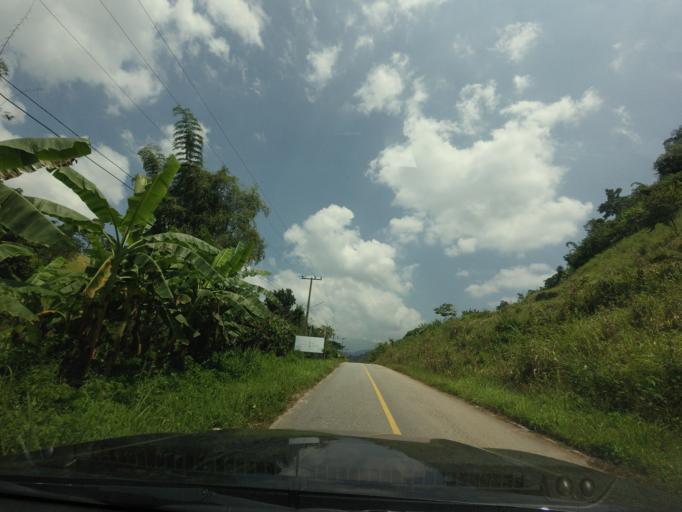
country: TH
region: Loei
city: Na Haeo
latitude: 17.6501
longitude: 100.9156
